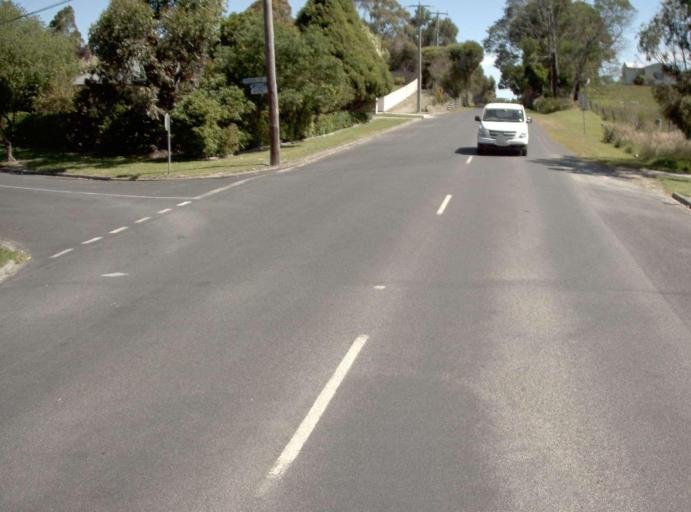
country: AU
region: Victoria
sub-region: Latrobe
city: Morwell
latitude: -38.6544
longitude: 146.1946
